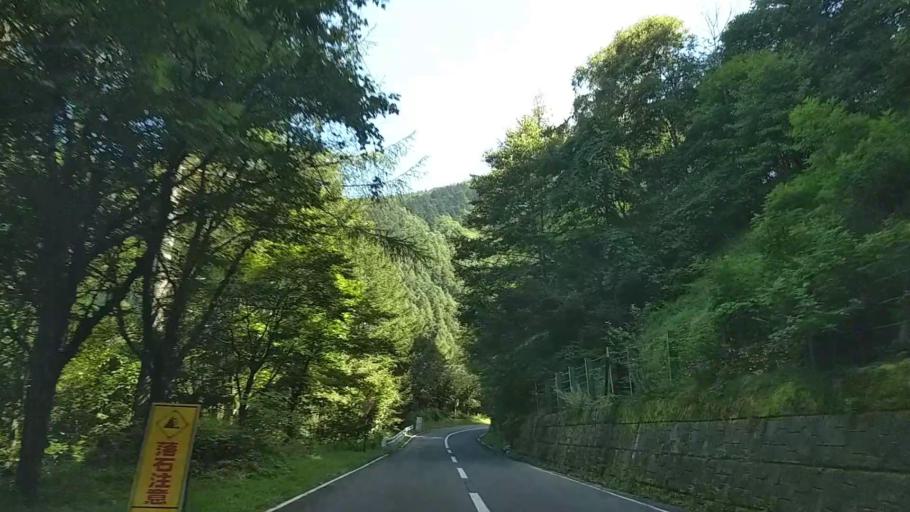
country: JP
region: Nagano
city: Matsumoto
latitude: 36.1975
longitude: 138.1150
